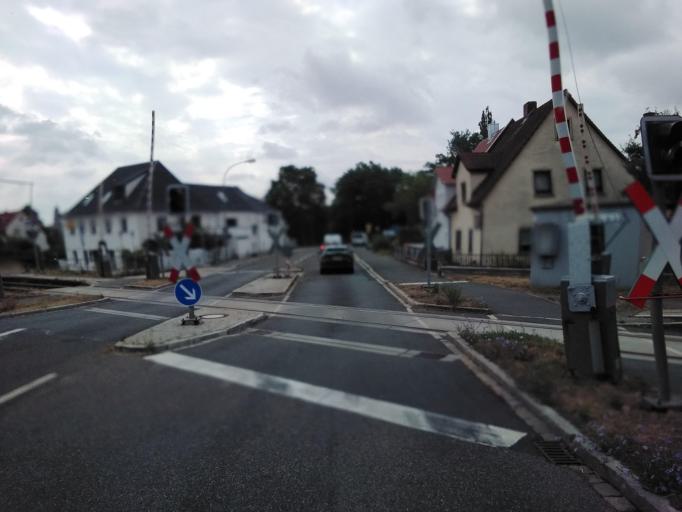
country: DE
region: Bavaria
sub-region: Regierungsbezirk Mittelfranken
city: Langenzenn
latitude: 49.4971
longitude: 10.7845
